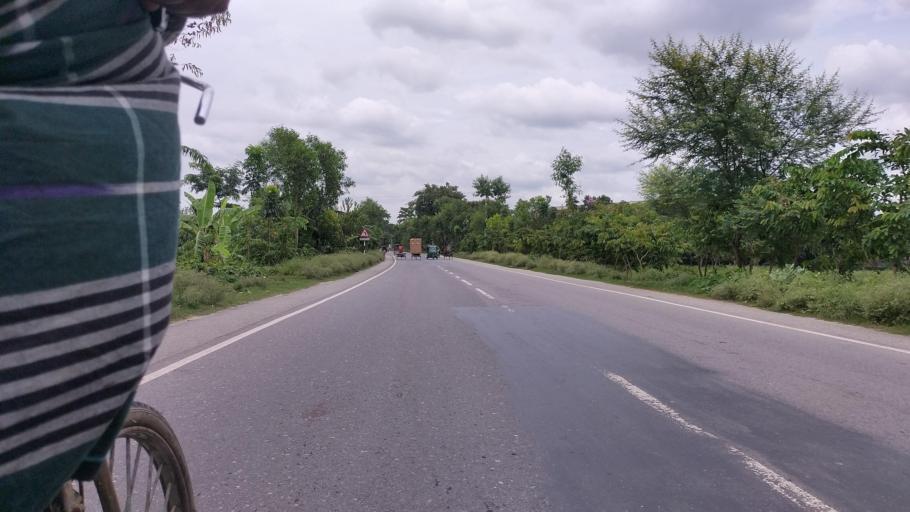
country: BD
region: Rajshahi
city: Rajshahi
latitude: 24.5109
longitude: 88.6336
